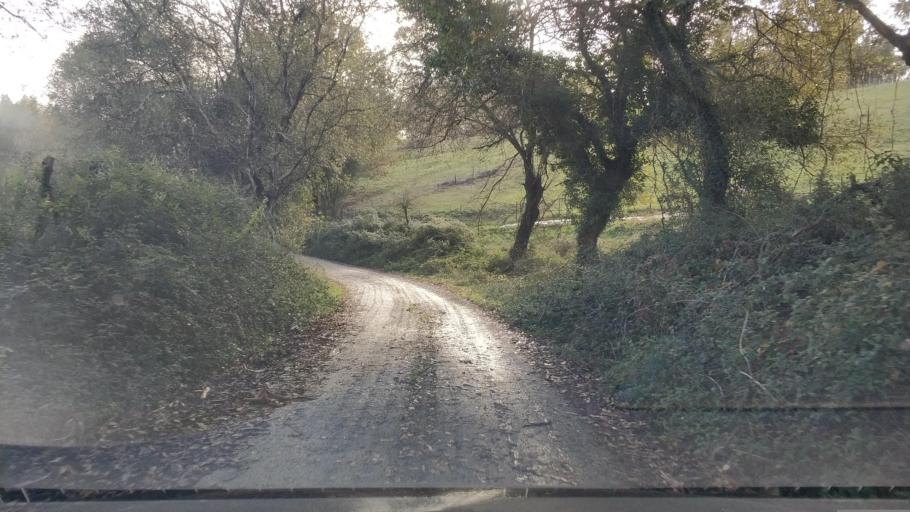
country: ES
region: Cantabria
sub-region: Provincia de Cantabria
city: Luzmela
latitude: 43.3385
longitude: -4.1859
